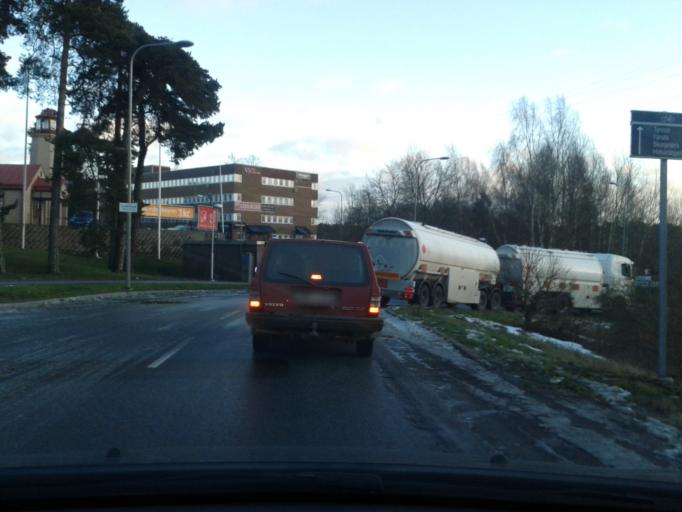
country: SE
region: Stockholm
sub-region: Stockholms Kommun
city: Arsta
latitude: 59.2620
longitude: 18.1035
